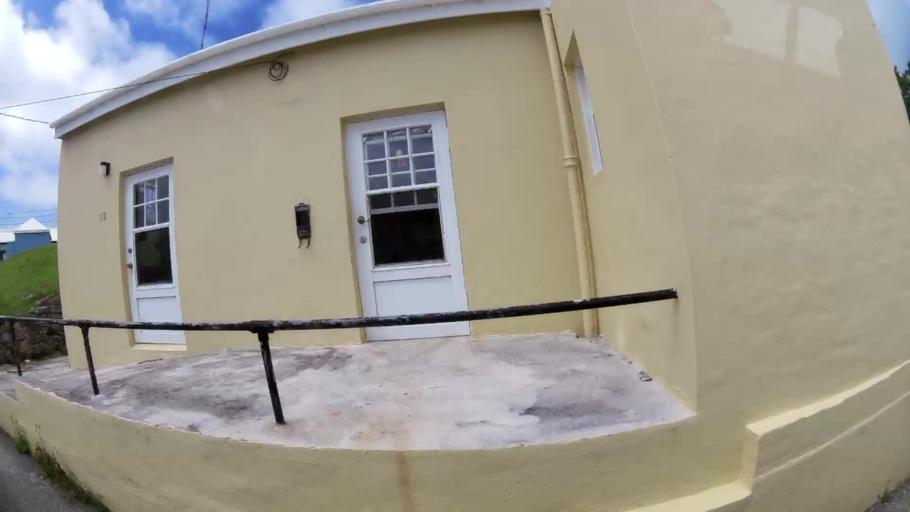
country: BM
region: Saint George
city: Saint George
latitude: 32.3685
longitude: -64.6495
